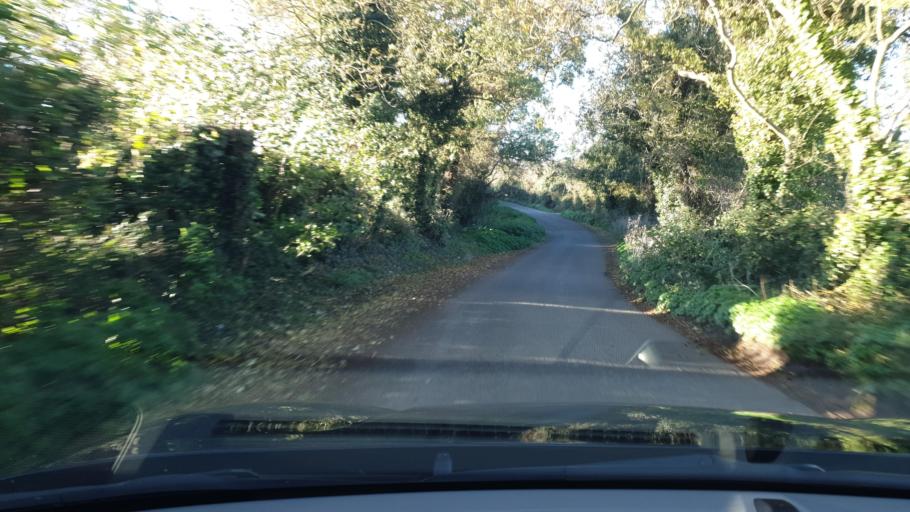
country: IE
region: Leinster
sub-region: An Mhi
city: Stamullin
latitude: 53.6541
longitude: -6.3002
